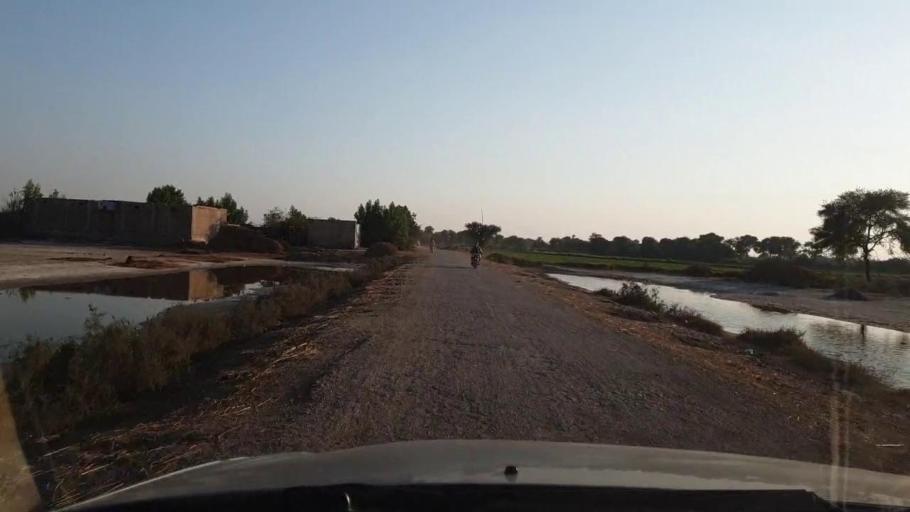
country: PK
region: Sindh
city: Matli
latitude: 25.0416
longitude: 68.6339
